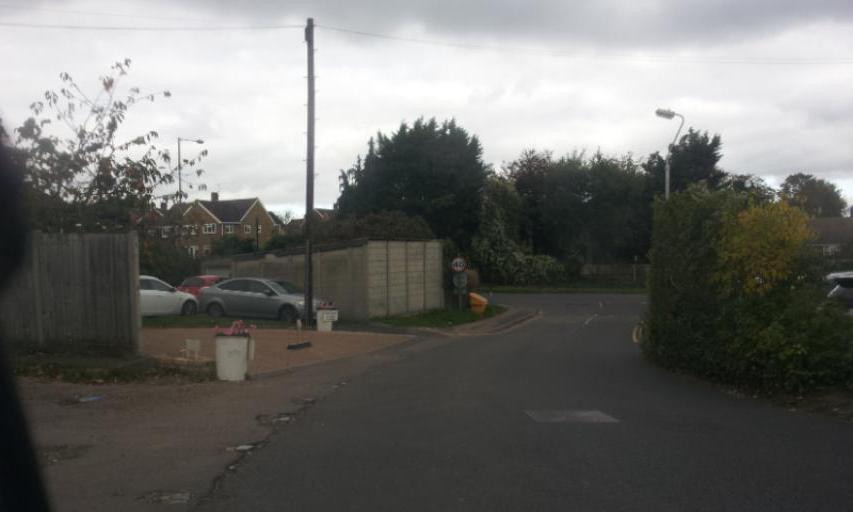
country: GB
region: England
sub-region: Kent
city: Larkfield
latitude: 51.2987
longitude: 0.4465
